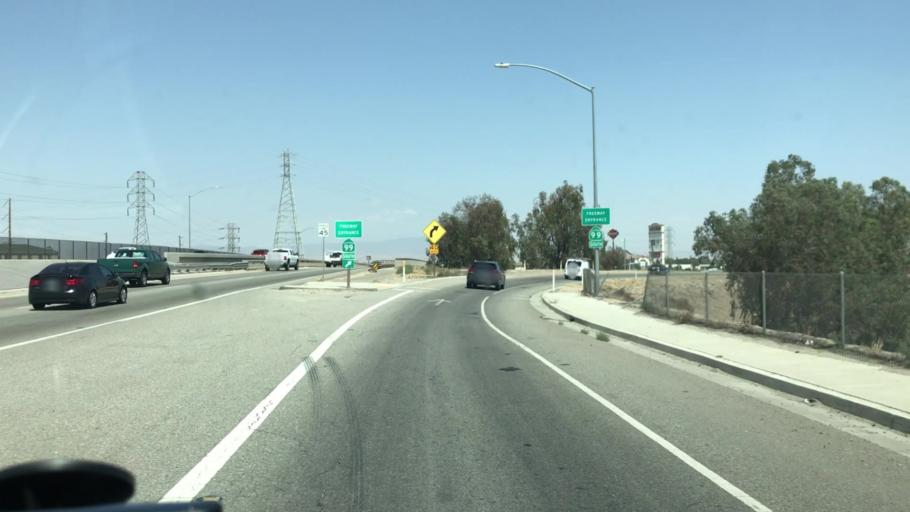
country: US
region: California
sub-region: Kern County
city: Greenacres
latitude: 35.4412
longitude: -119.0855
